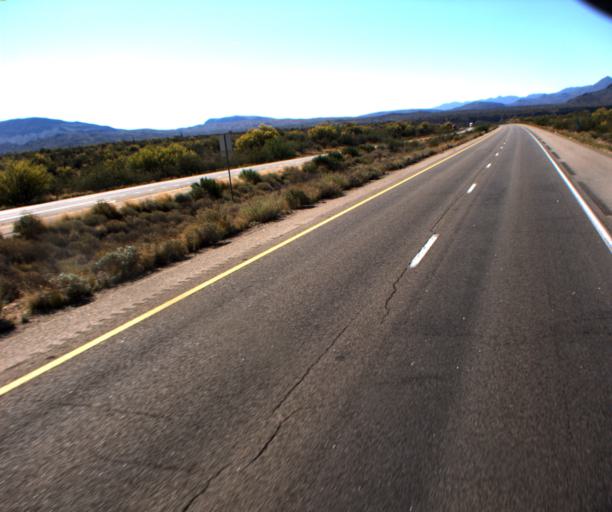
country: US
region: Arizona
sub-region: Yavapai County
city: Bagdad
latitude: 34.6520
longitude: -113.5731
